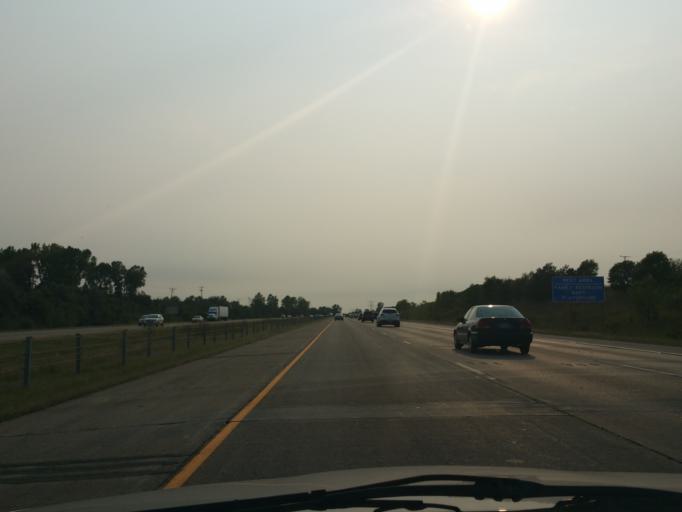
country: US
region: Minnesota
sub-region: Washington County
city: Lakeland
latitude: 44.9542
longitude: -92.7988
